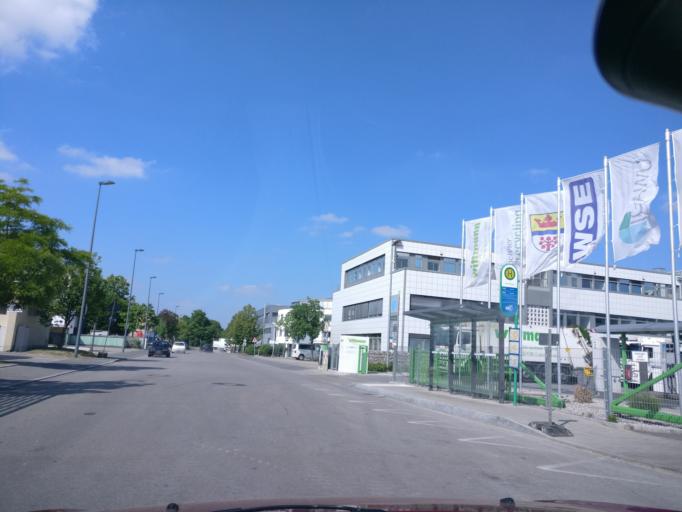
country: DE
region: Bavaria
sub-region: Upper Bavaria
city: Pasing
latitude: 48.1231
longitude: 11.4513
